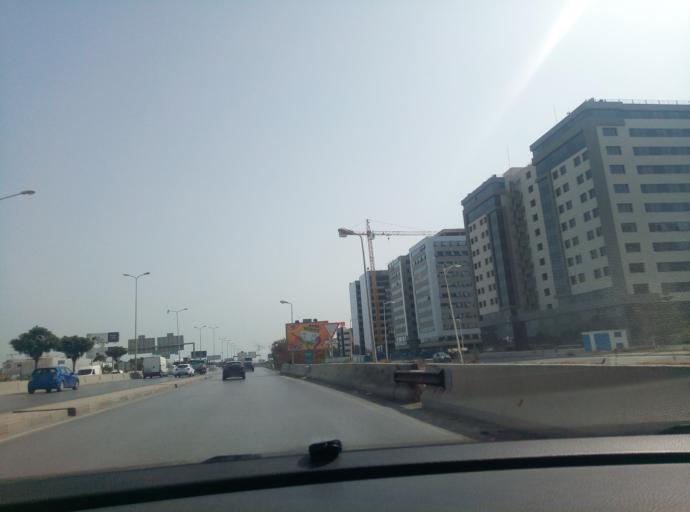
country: TN
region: Ariana
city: Ariana
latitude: 36.8470
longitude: 10.2018
